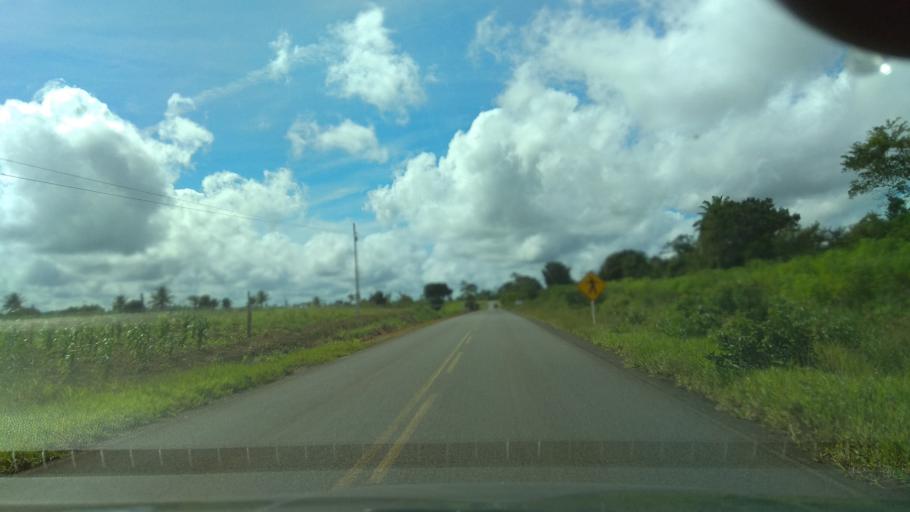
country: BR
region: Bahia
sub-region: Mutuipe
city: Mutuipe
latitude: -13.1671
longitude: -39.3392
